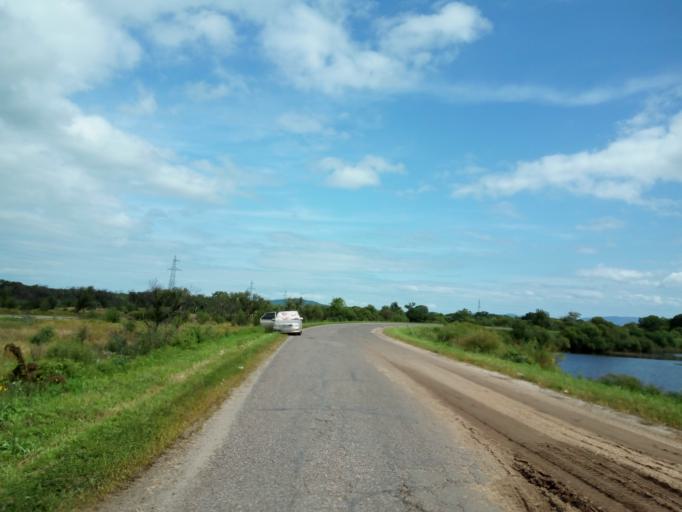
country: RU
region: Primorskiy
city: Dal'nerechensk
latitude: 45.9693
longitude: 133.7778
